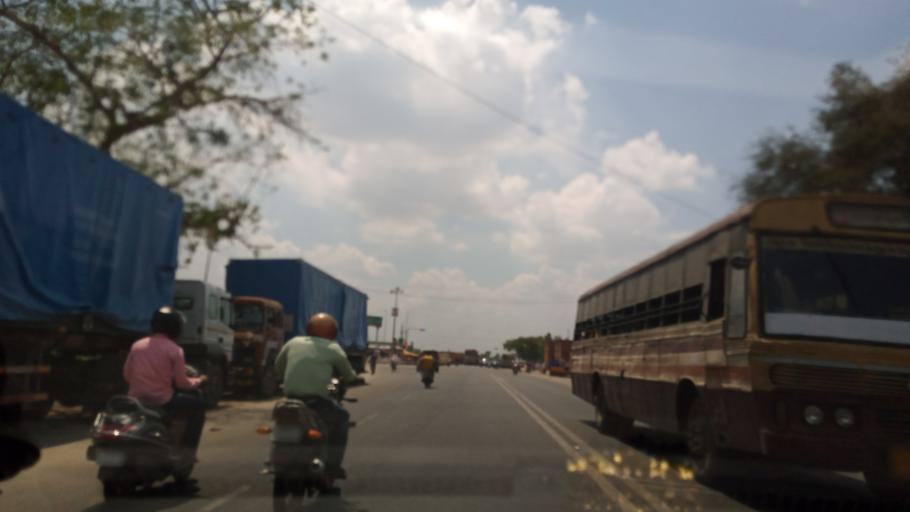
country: IN
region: Tamil Nadu
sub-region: Vellore
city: Walajapet
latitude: 12.9264
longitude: 79.3499
